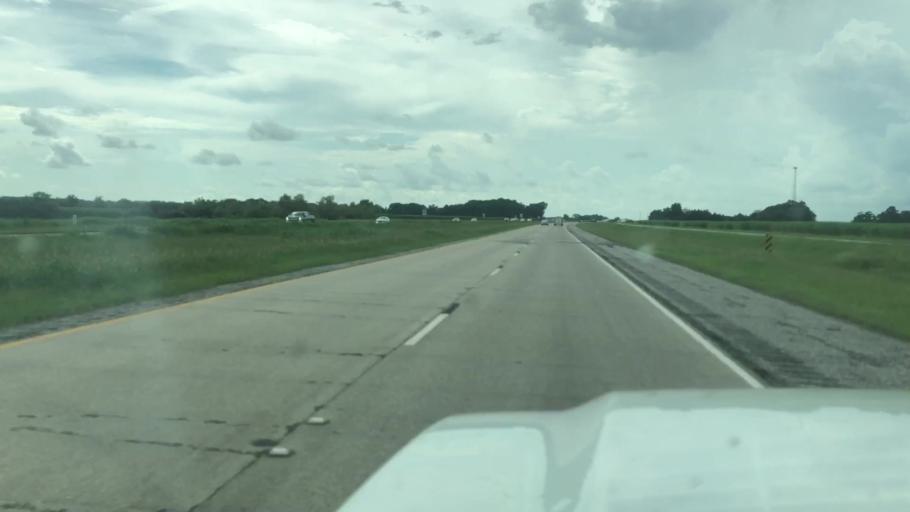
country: US
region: Louisiana
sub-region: Iberia Parish
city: Jeanerette
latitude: 29.8595
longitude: -91.6178
